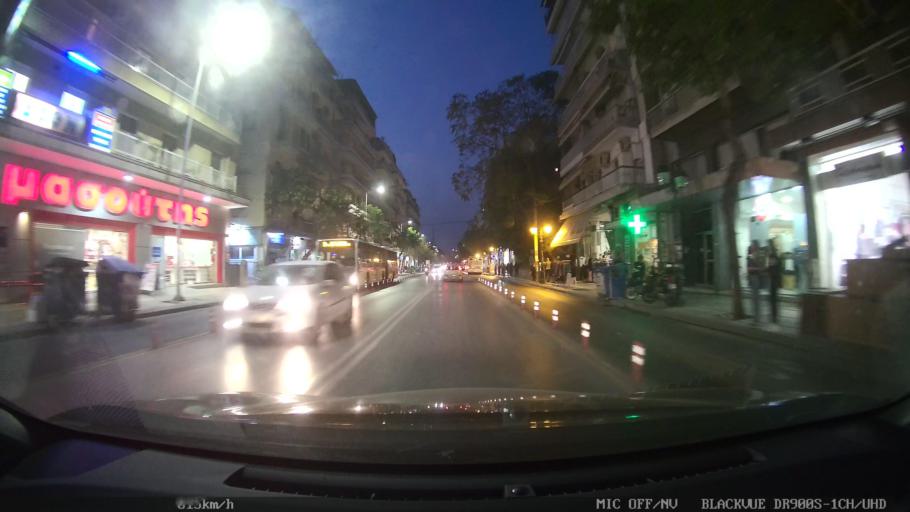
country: GR
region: Central Macedonia
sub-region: Nomos Thessalonikis
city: Triandria
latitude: 40.6194
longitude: 22.9581
